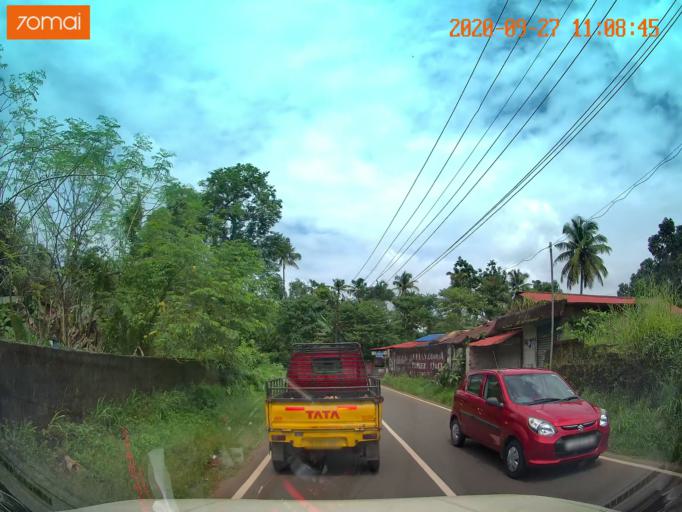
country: IN
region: Kerala
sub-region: Thrissur District
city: Trichur
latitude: 10.4317
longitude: 76.2318
